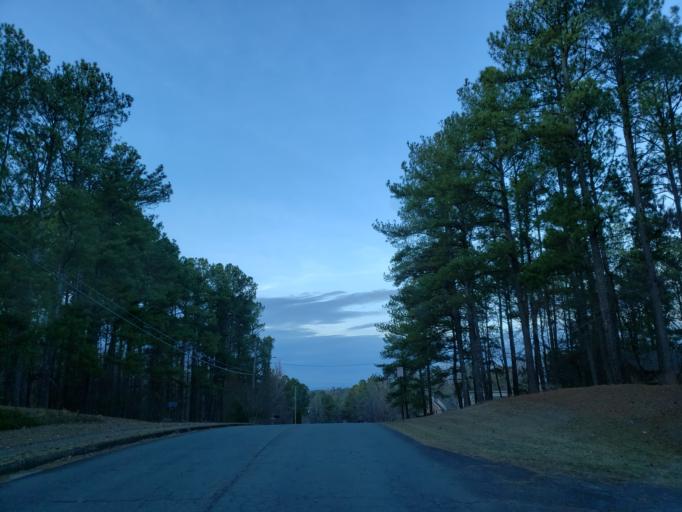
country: US
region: Georgia
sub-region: Cobb County
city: Kennesaw
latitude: 34.0434
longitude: -84.6451
